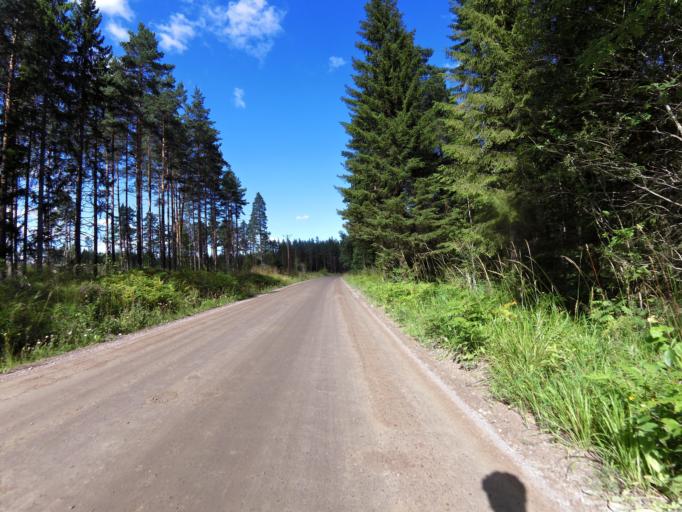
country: SE
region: Gaevleborg
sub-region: Hofors Kommun
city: Hofors
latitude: 60.5105
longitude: 16.3176
